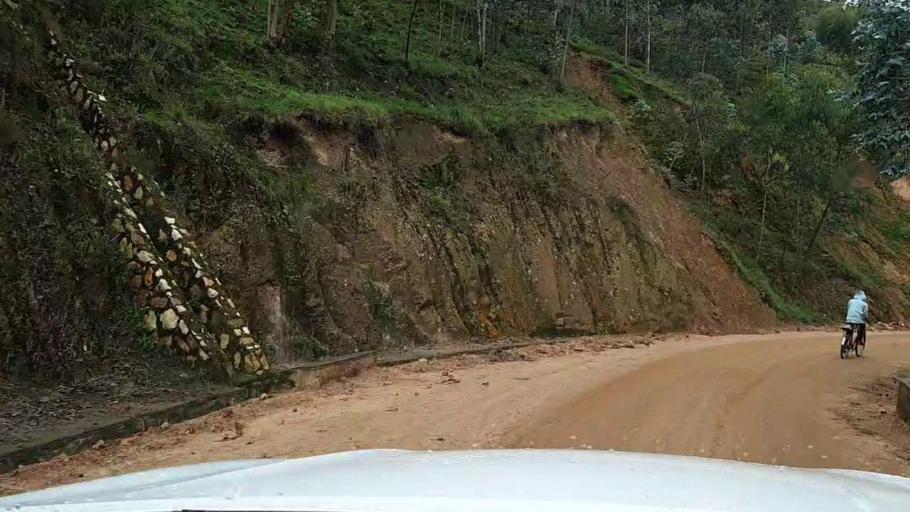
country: RW
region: Southern Province
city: Nzega
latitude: -2.4537
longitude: 29.4659
